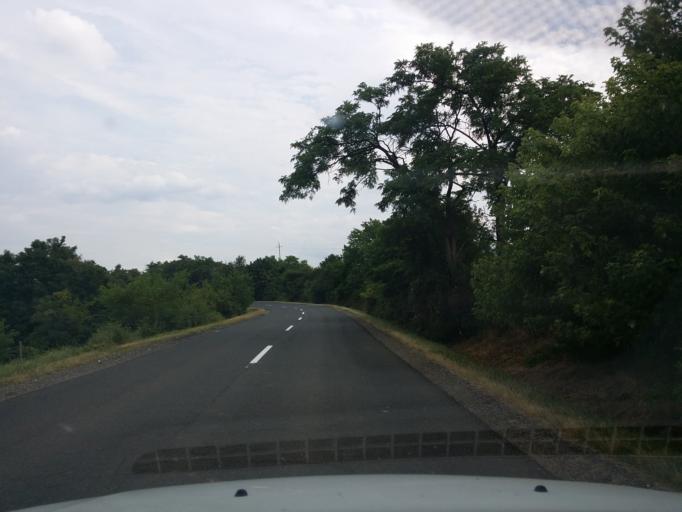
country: HU
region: Nograd
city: Bercel
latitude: 47.9244
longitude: 19.3636
